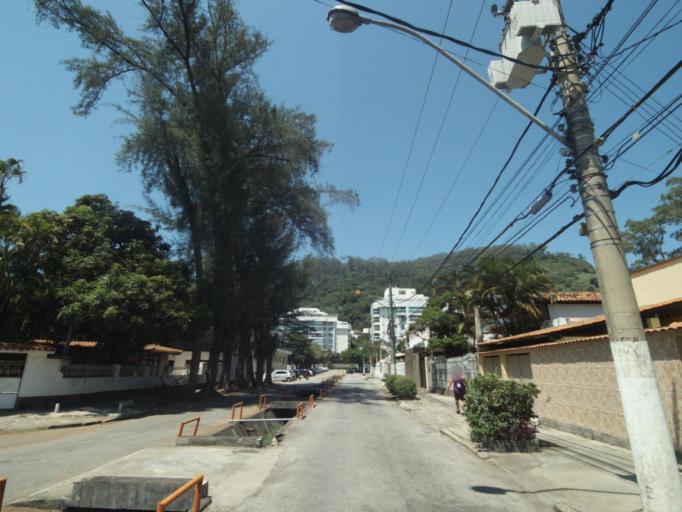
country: BR
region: Rio de Janeiro
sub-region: Niteroi
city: Niteroi
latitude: -22.9216
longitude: -43.0933
